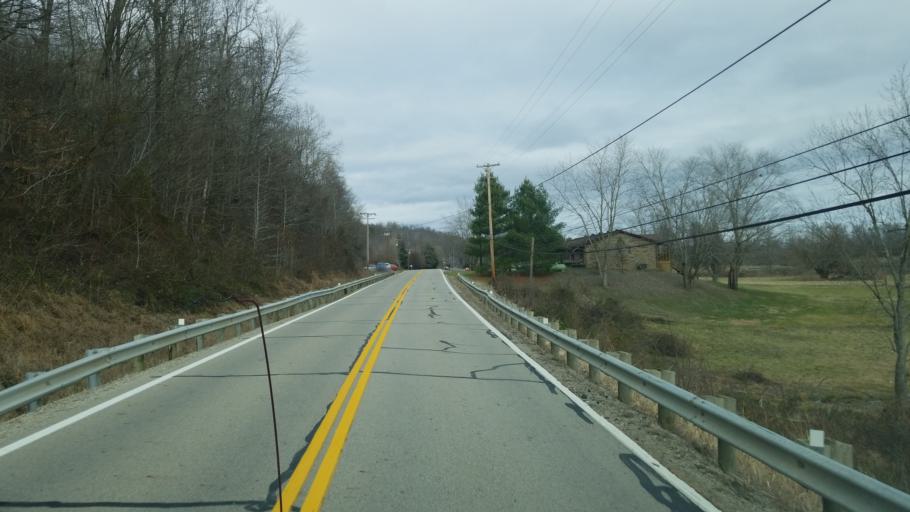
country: US
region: Ohio
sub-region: Scioto County
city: West Portsmouth
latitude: 38.6552
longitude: -83.1319
